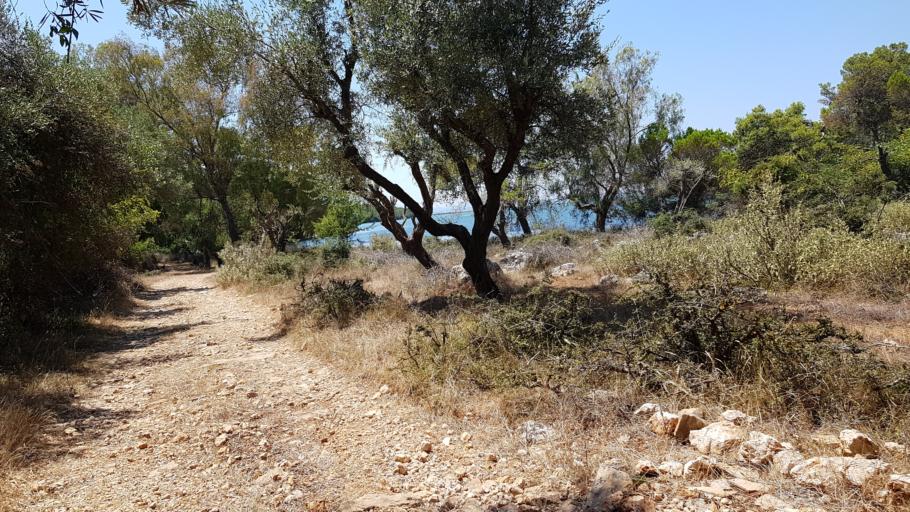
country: AL
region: Vlore
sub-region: Rrethi i Sarandes
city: Xarre
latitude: 39.7536
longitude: 19.9998
